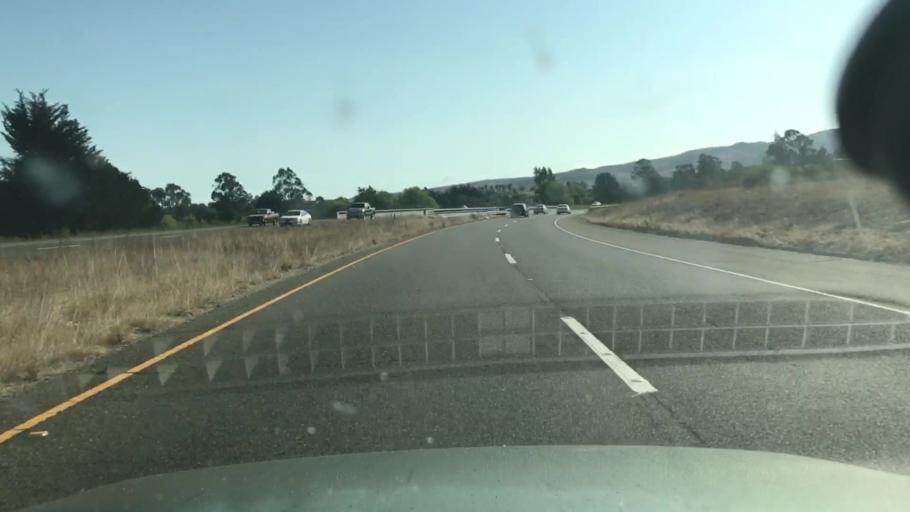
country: US
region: California
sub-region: Santa Barbara County
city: Orcutt
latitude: 34.8605
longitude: -120.4376
